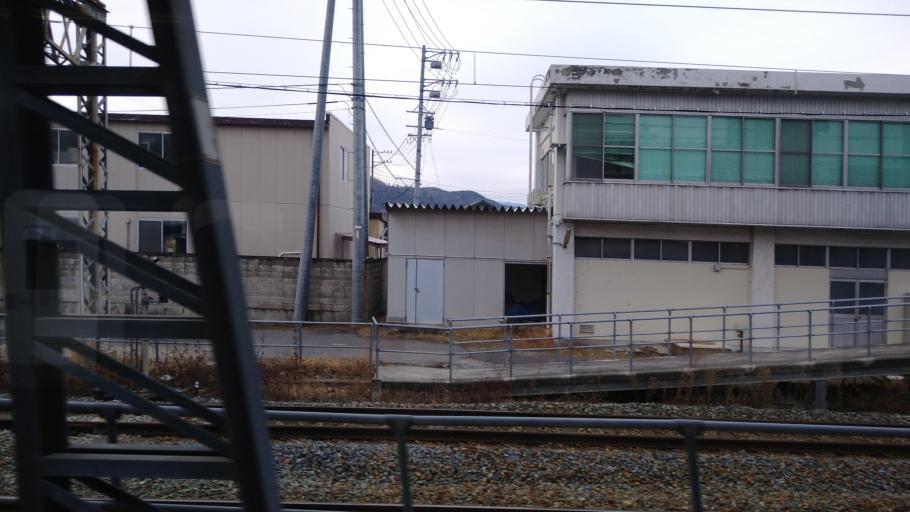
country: JP
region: Nagano
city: Ueda
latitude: 36.3951
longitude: 138.2510
